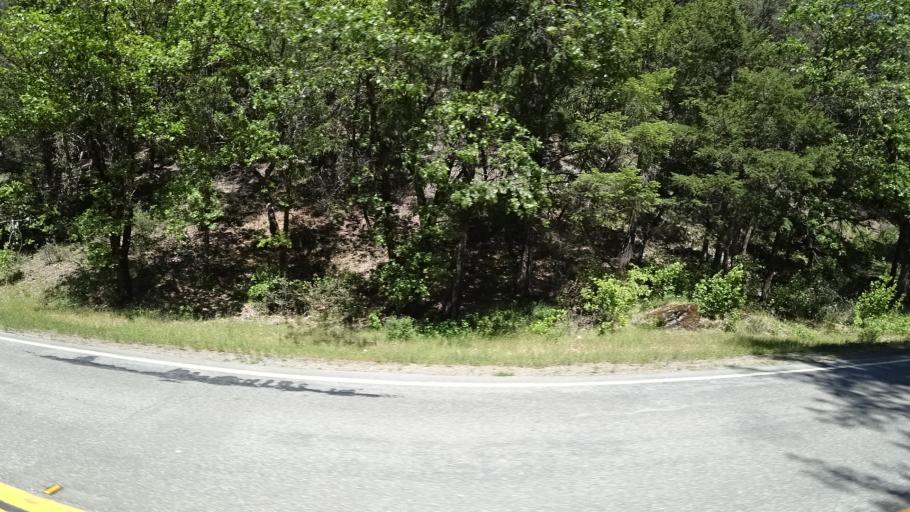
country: US
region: California
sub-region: Trinity County
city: Hayfork
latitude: 40.7511
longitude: -123.2793
